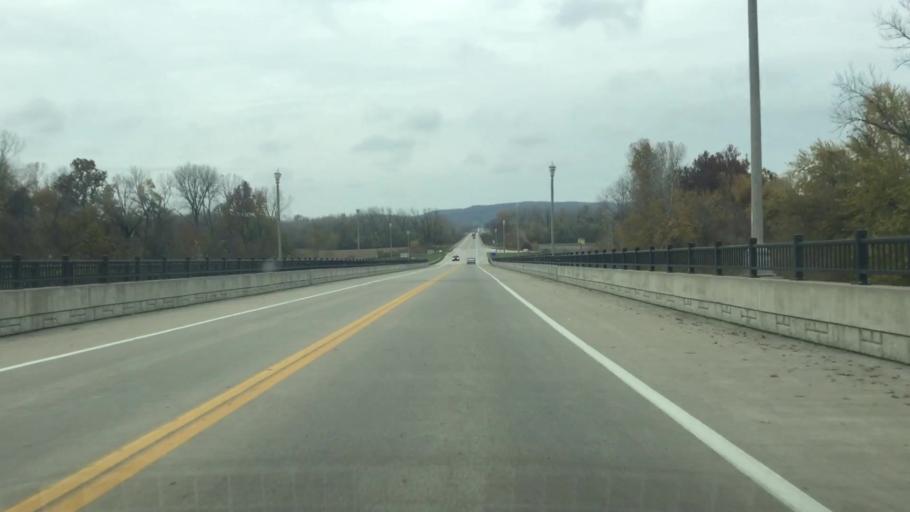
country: US
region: Missouri
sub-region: Gasconade County
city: Hermann
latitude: 38.7116
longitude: -91.4396
